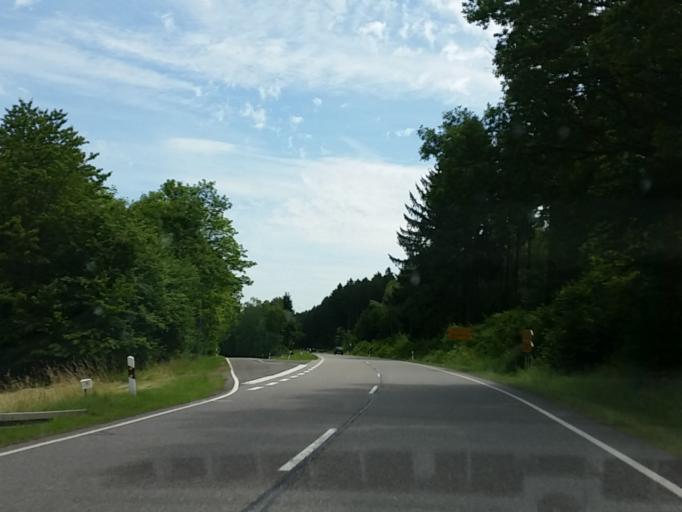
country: DE
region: Saarland
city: Britten
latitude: 49.5250
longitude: 6.6961
